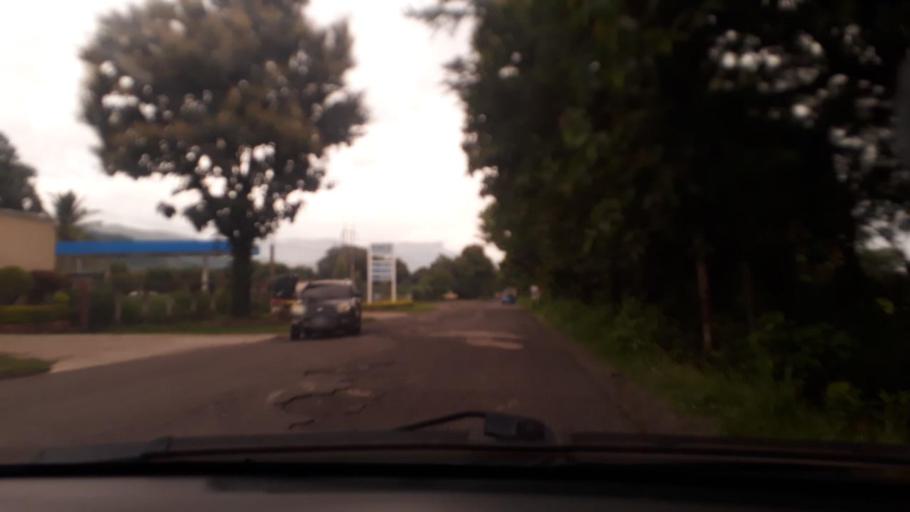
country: GT
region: Jutiapa
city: Jalpatagua
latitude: 14.1513
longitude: -90.0409
